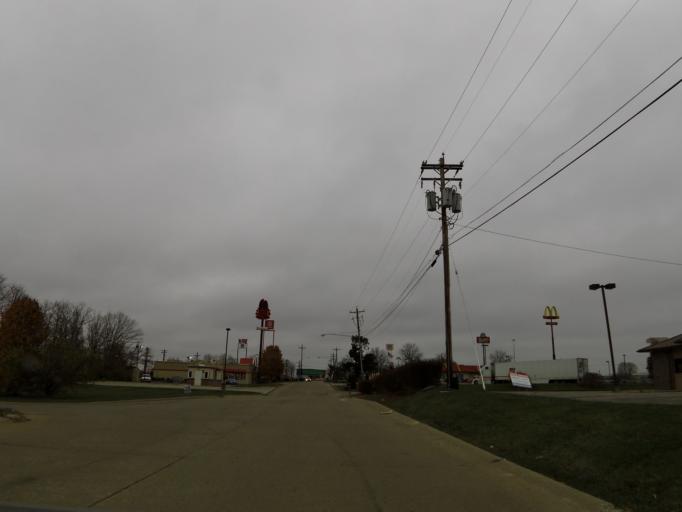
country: US
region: Kentucky
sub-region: Grant County
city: Dry Ridge
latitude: 38.6845
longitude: -84.5996
